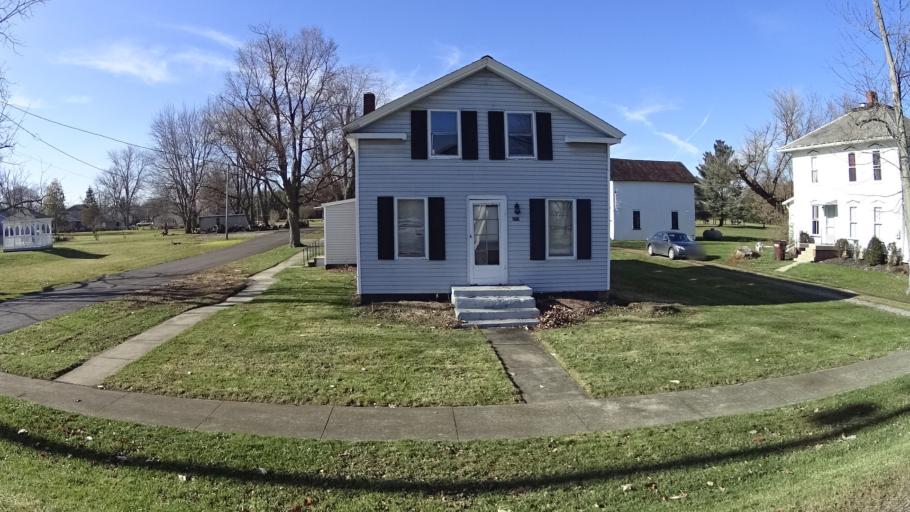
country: US
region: Ohio
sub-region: Lorain County
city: Wellington
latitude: 41.1267
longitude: -82.3048
